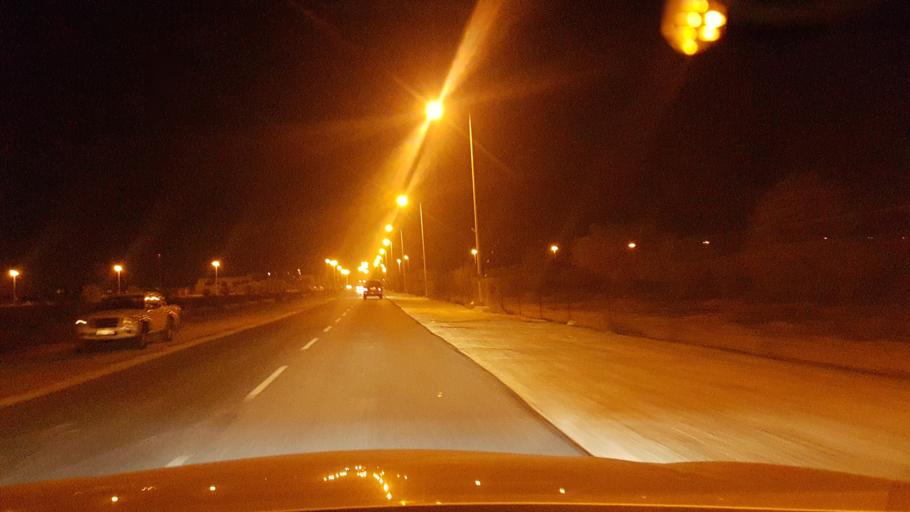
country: BH
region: Central Governorate
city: Dar Kulayb
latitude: 26.0192
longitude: 50.4839
